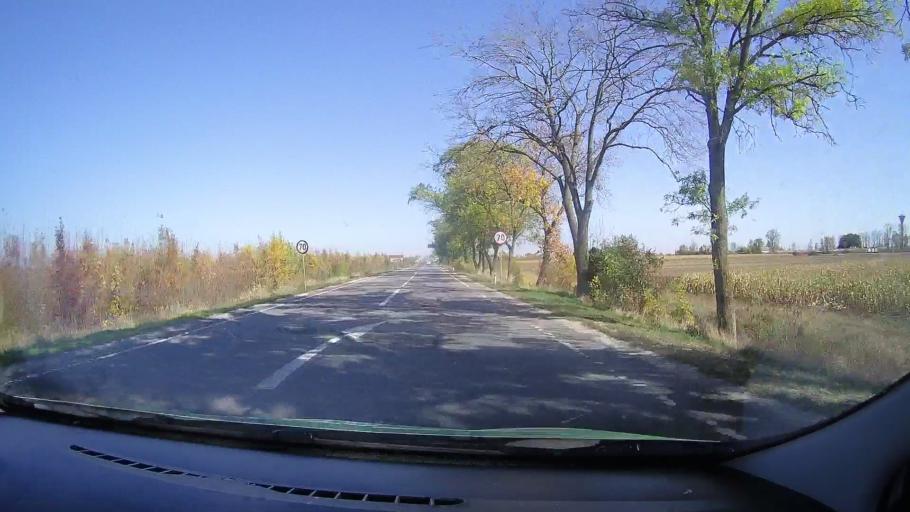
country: RO
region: Satu Mare
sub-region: Comuna Moftinu
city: Moftinu Mic
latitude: 47.7037
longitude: 22.6323
